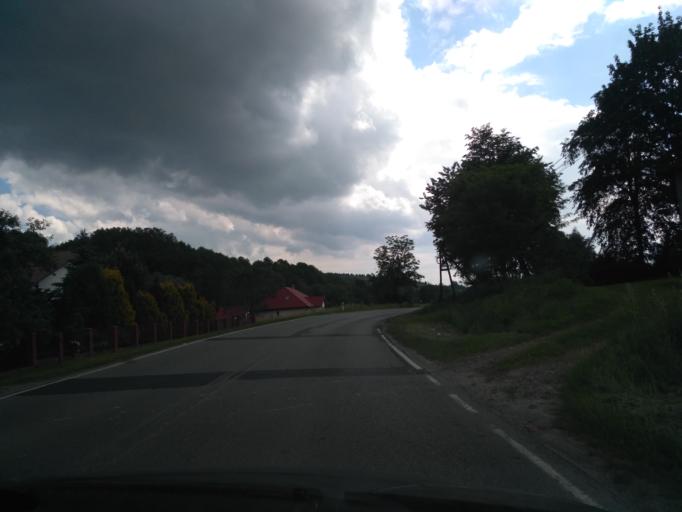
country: PL
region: Subcarpathian Voivodeship
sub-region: Powiat rzeszowski
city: Blazowa
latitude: 49.9371
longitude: 22.1071
